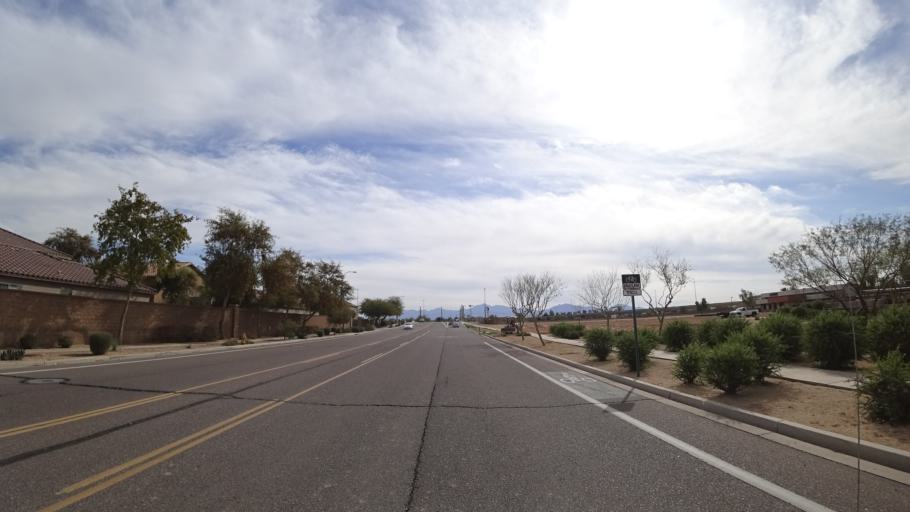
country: US
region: Arizona
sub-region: Maricopa County
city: Tolleson
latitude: 33.4667
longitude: -112.2640
